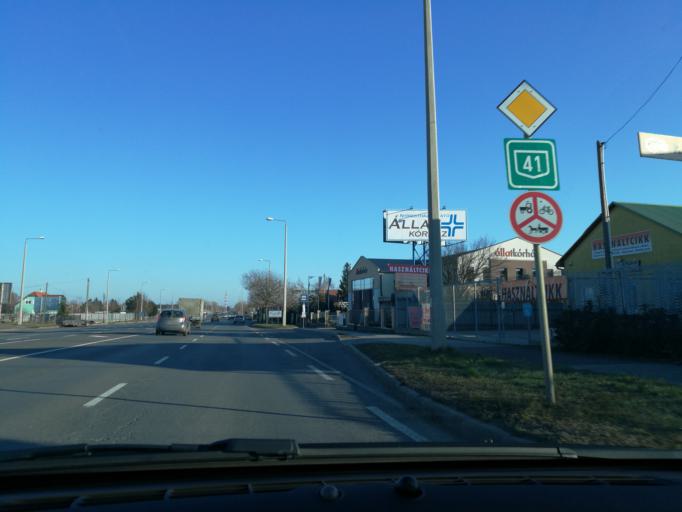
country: HU
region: Szabolcs-Szatmar-Bereg
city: Nyirpazony
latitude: 47.9507
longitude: 21.7671
